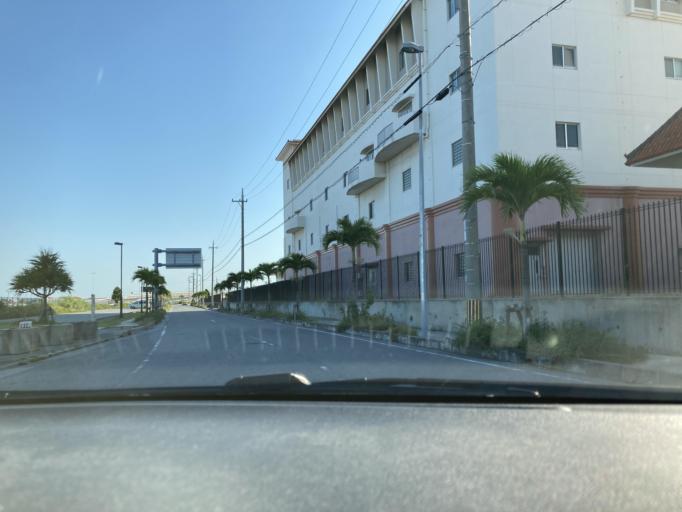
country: JP
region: Okinawa
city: Naha-shi
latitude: 26.2180
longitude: 127.6637
